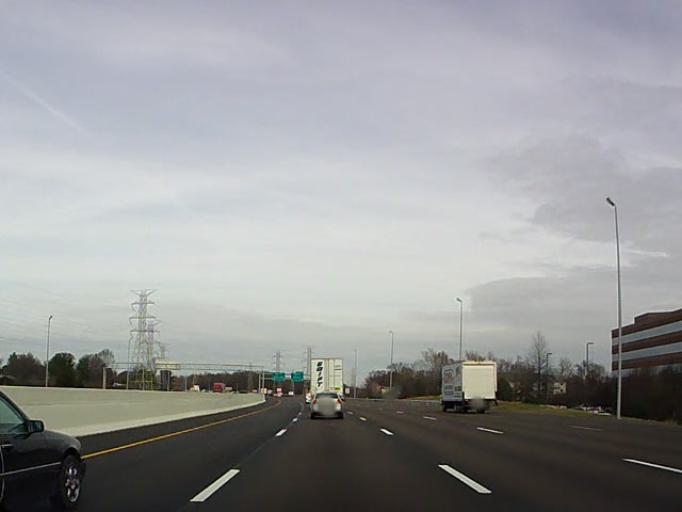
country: US
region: Tennessee
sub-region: Shelby County
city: Bartlett
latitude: 35.1350
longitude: -89.8676
